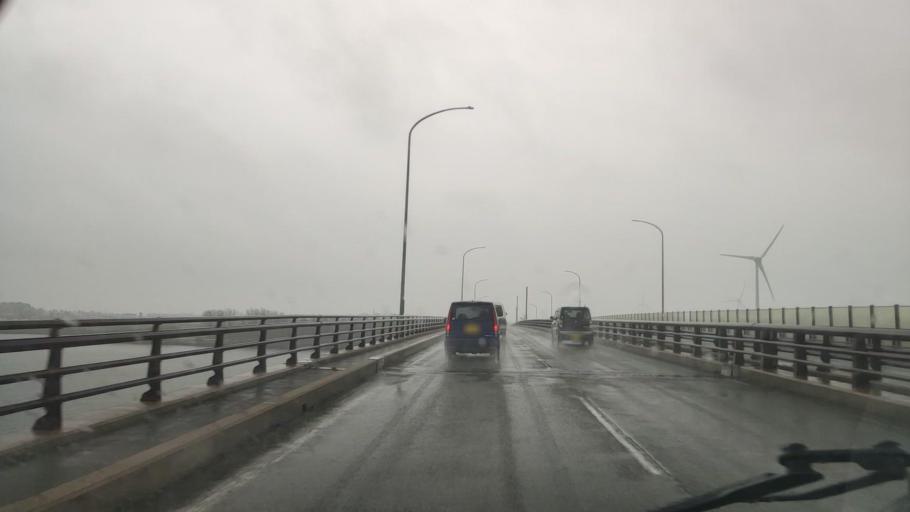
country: JP
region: Akita
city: Tenno
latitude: 39.8965
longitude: 139.9506
